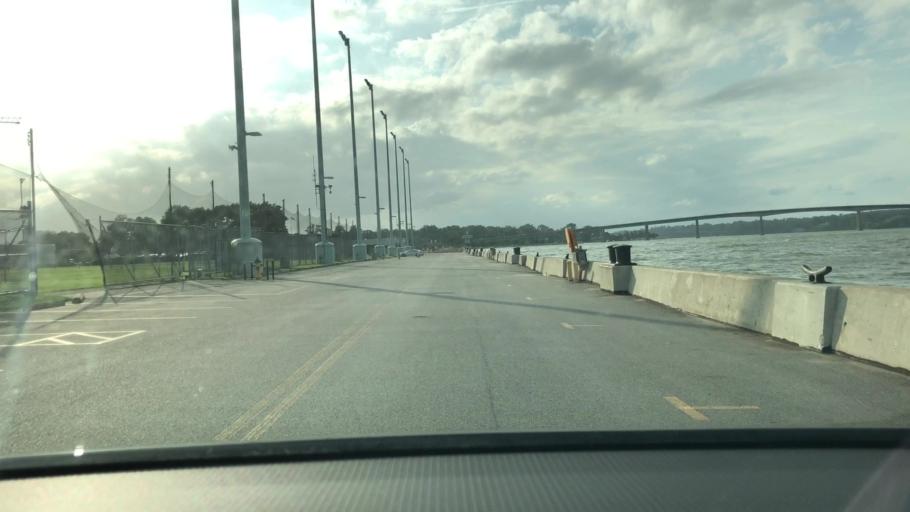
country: US
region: Maryland
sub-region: Anne Arundel County
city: Naval Academy
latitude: 38.9852
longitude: -76.4820
